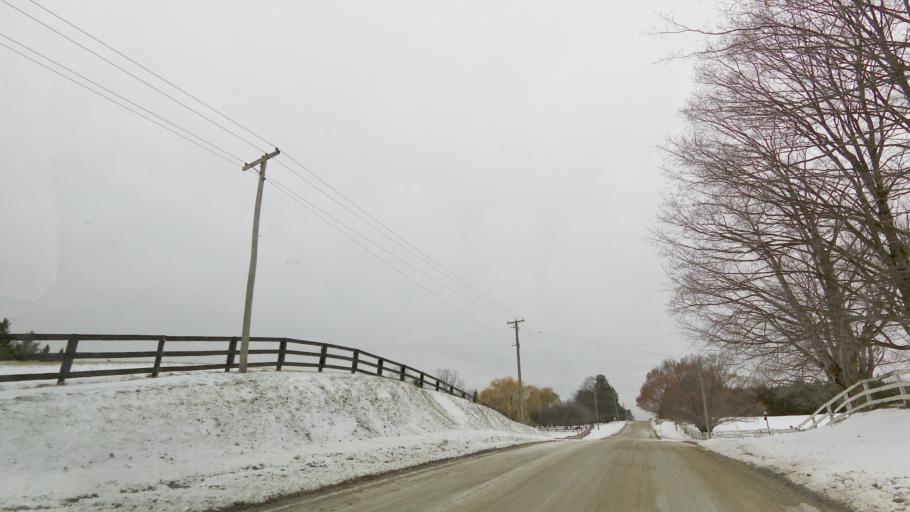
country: CA
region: Ontario
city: Vaughan
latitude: 43.9463
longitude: -79.6263
